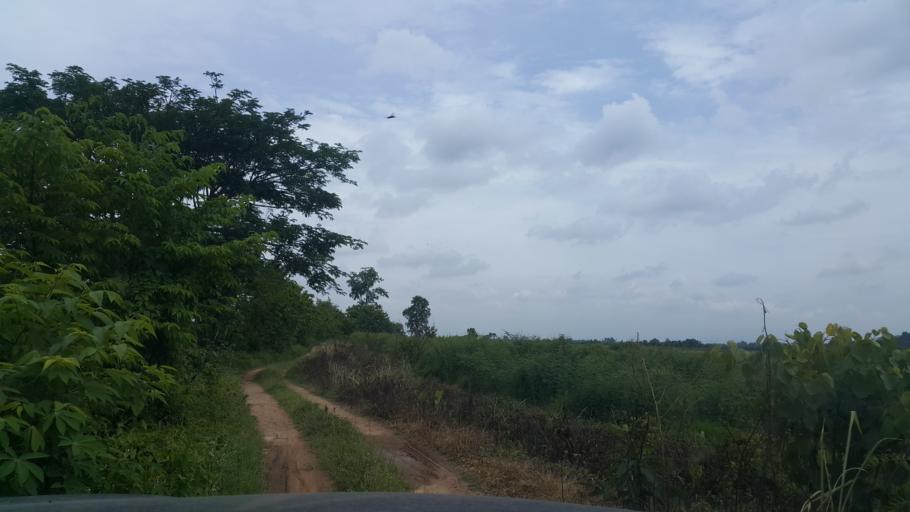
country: TH
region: Lamphun
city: Ban Thi
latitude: 18.6320
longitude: 99.1577
